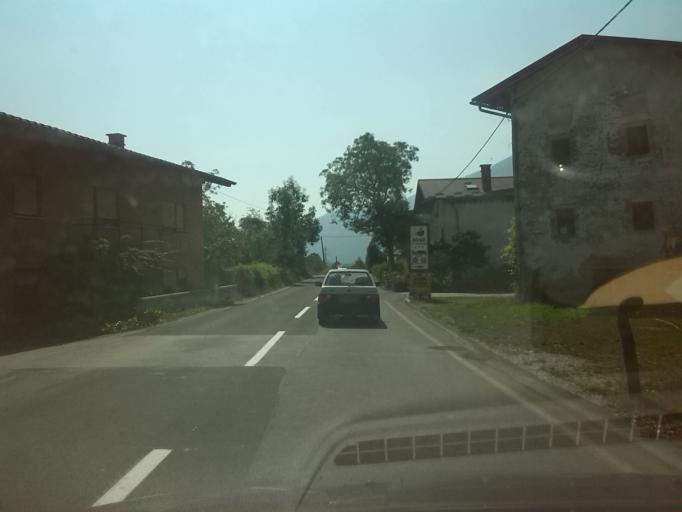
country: SI
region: Kobarid
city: Kobarid
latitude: 46.2315
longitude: 13.5935
